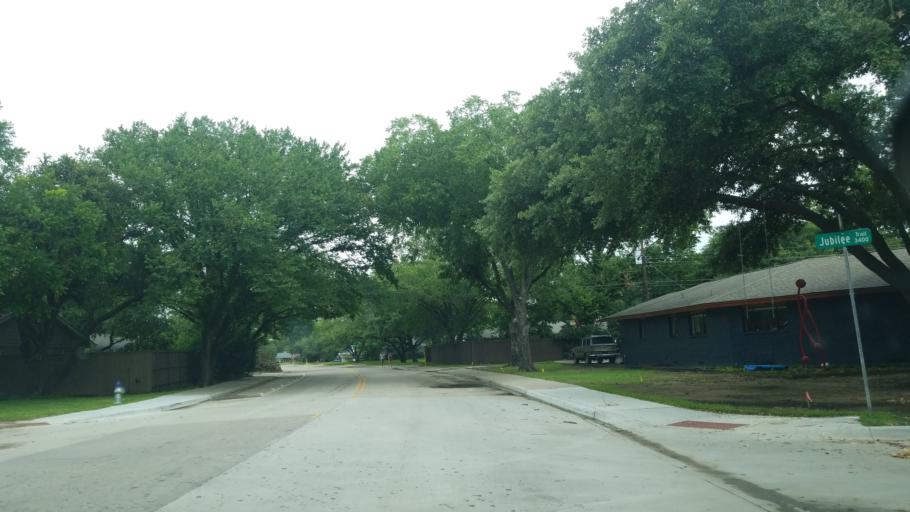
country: US
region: Texas
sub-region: Dallas County
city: Farmers Branch
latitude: 32.9004
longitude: -96.8624
